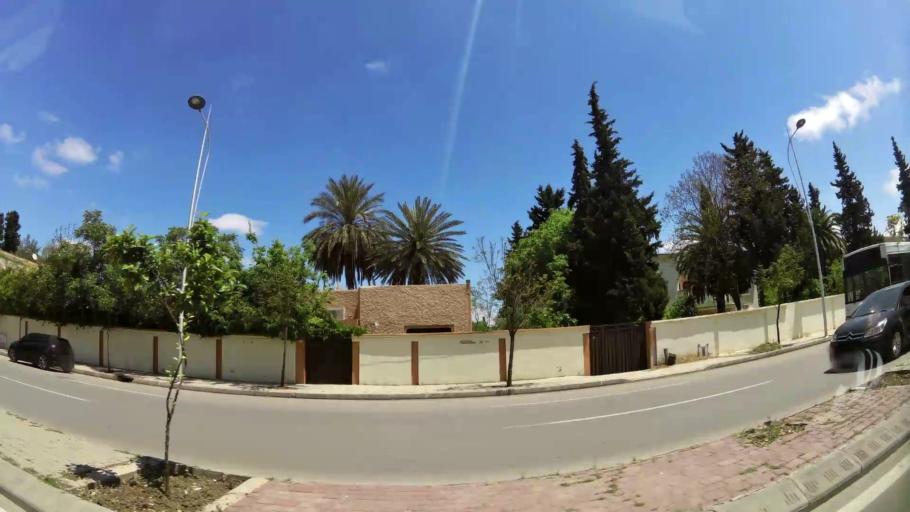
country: MA
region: Fes-Boulemane
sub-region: Fes
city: Fes
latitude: 34.0209
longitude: -4.9965
